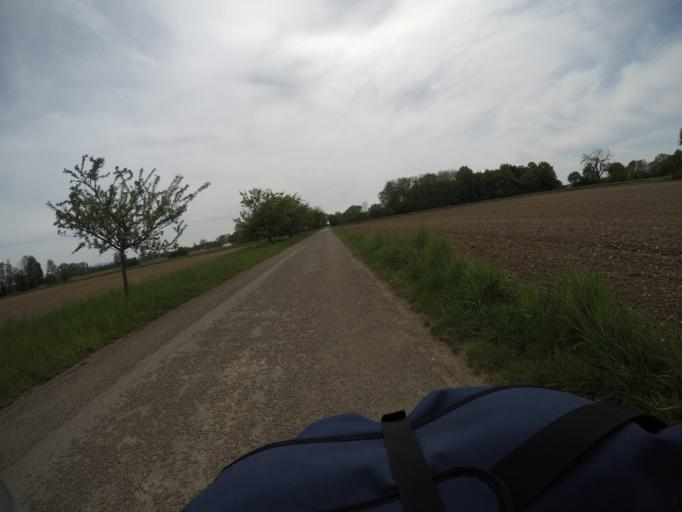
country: DE
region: Baden-Wuerttemberg
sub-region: Freiburg Region
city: Kehl
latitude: 48.5929
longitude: 7.8412
